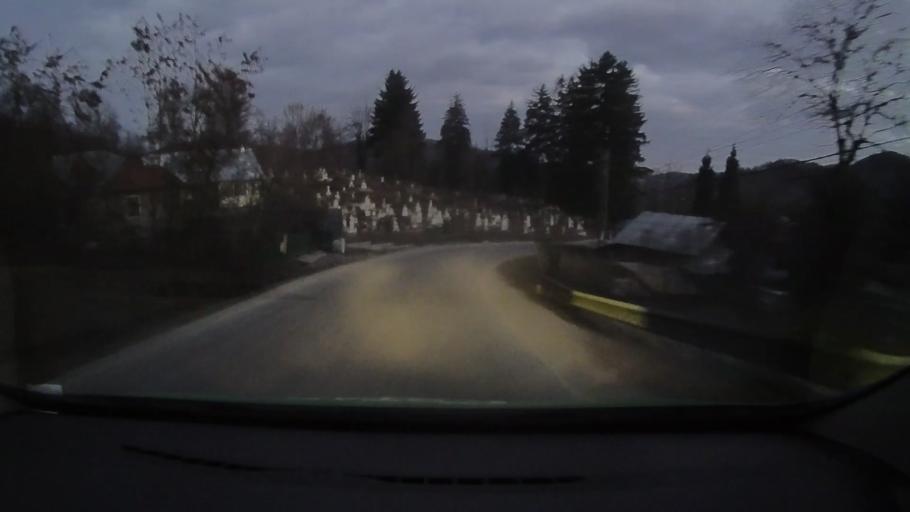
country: RO
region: Prahova
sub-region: Comuna Provita de Jos
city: Provita de Jos
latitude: 45.1225
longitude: 25.6615
